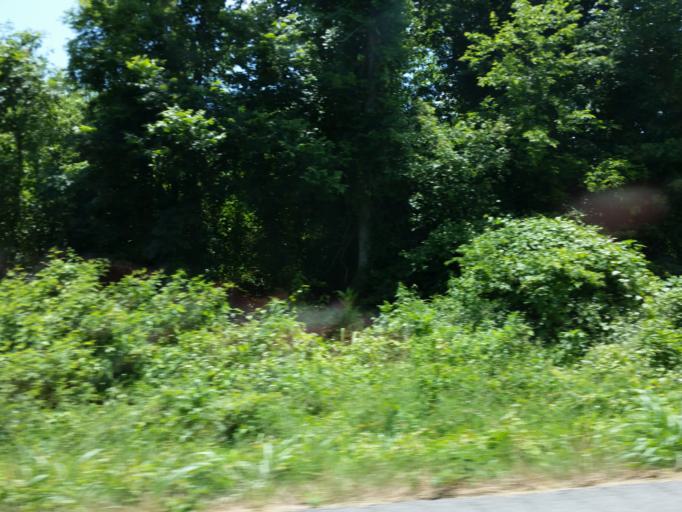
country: US
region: Kentucky
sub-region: Fulton County
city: Hickman
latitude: 36.5144
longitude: -89.3453
